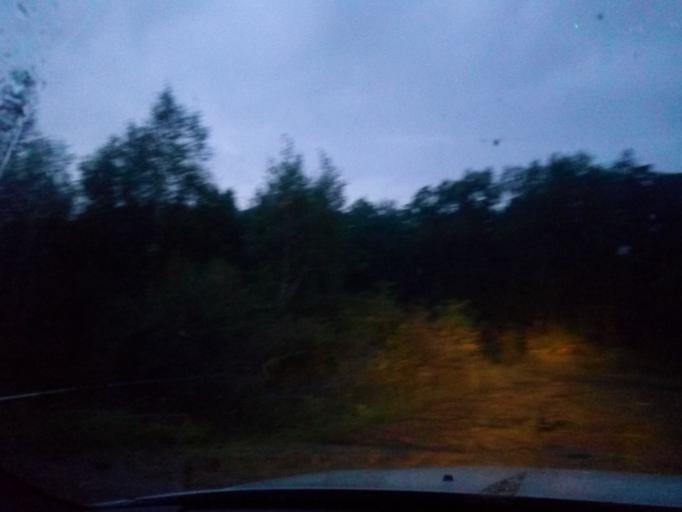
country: RU
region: Primorskiy
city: Dal'nerechensk
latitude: 45.8829
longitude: 133.7230
